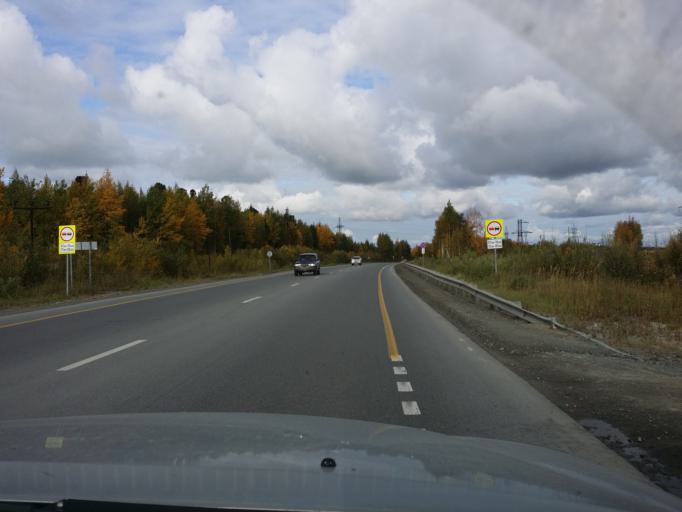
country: RU
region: Khanty-Mansiyskiy Avtonomnyy Okrug
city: Nizhnevartovsk
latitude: 61.0224
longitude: 76.3746
